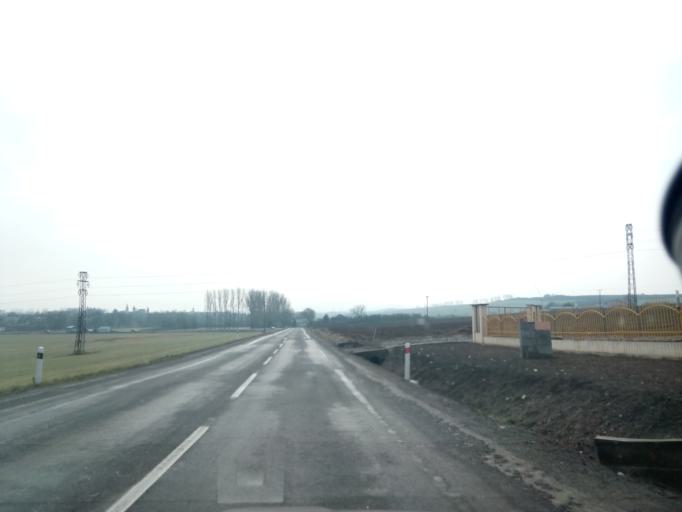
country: SK
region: Kosicky
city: Secovce
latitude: 48.6104
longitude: 21.6164
